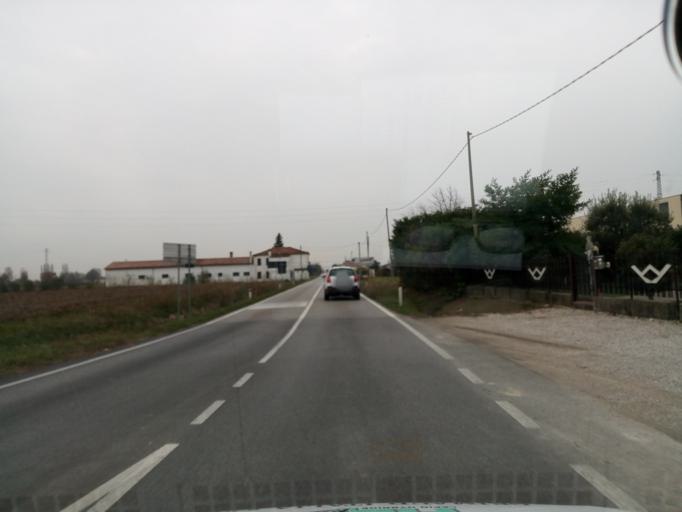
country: IT
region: Veneto
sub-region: Provincia di Padova
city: Villanova
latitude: 45.5026
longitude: 11.9729
